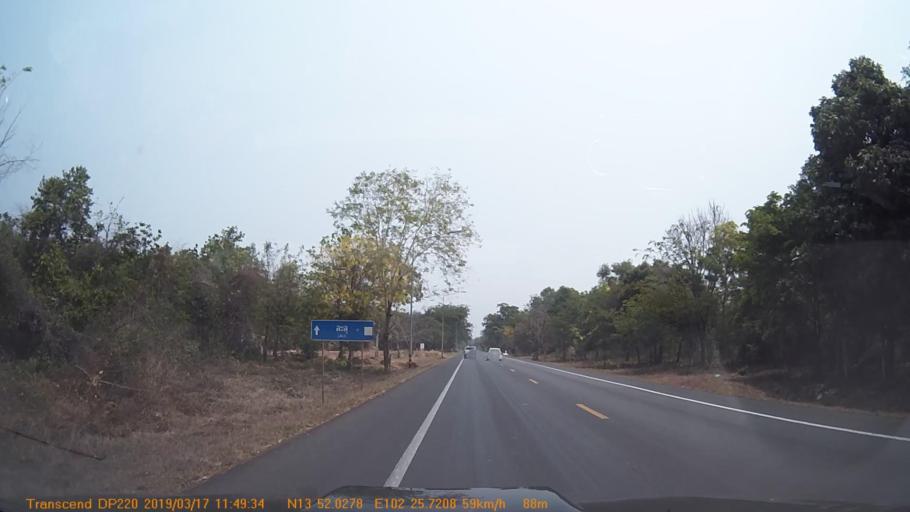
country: TH
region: Sa Kaeo
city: Watthana Nakhon
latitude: 13.8672
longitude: 102.4289
